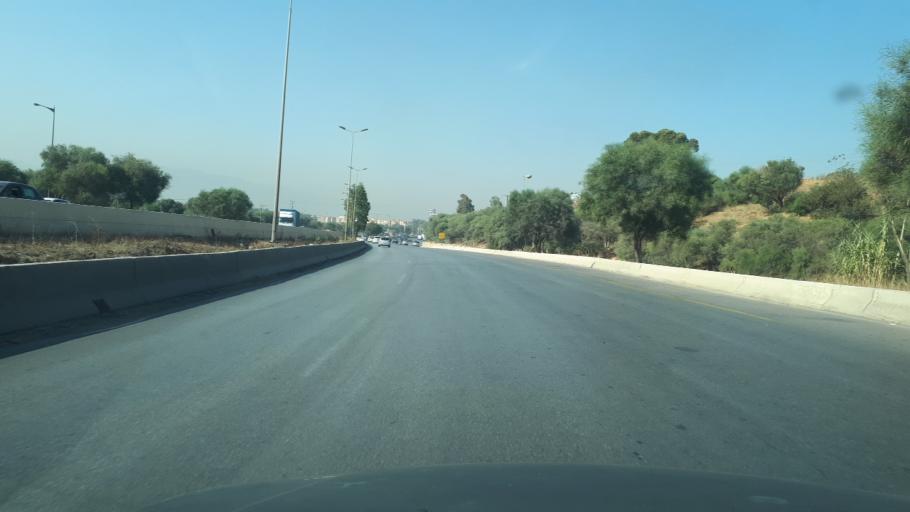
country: DZ
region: Alger
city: Birkhadem
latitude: 36.6774
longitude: 3.0580
